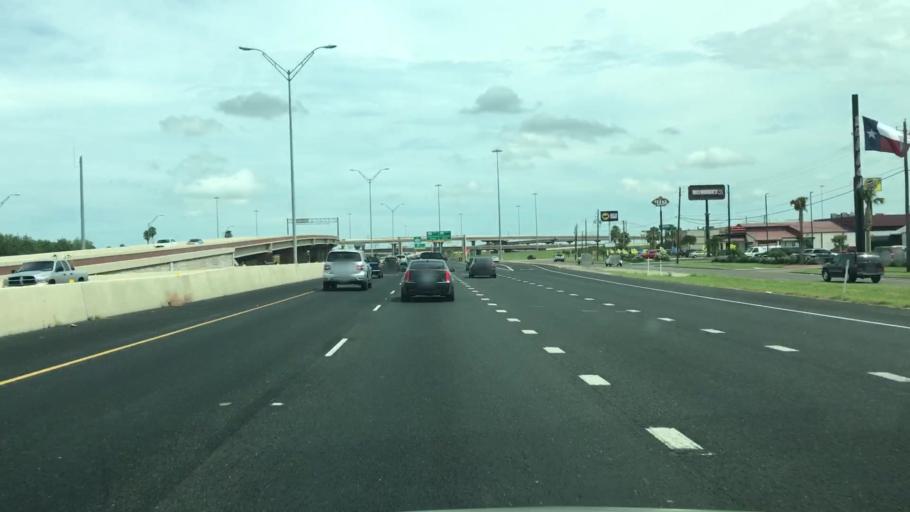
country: US
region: Texas
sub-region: Nueces County
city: Corpus Christi
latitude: 27.7402
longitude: -97.4369
